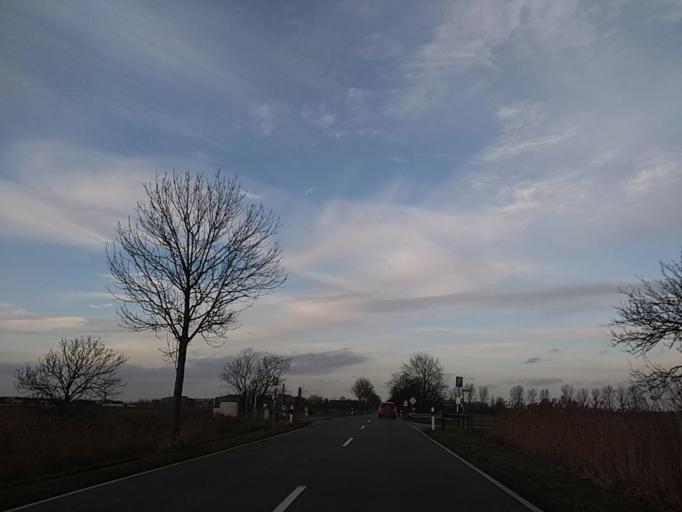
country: DE
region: Lower Saxony
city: Jemgum
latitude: 53.2441
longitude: 7.3909
